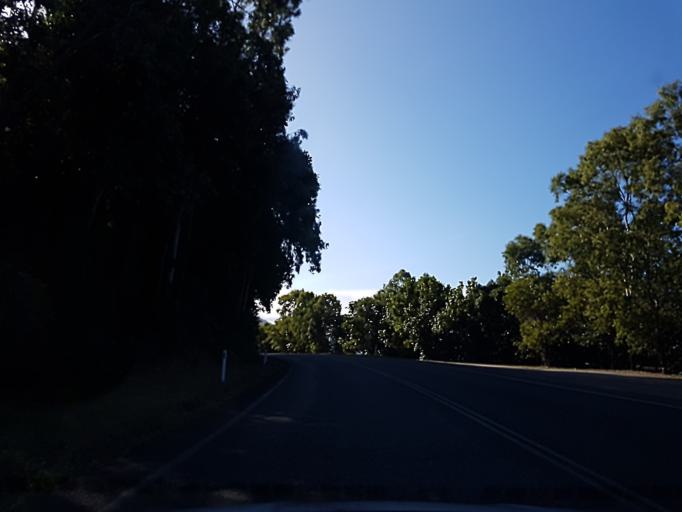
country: AU
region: Queensland
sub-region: Cairns
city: Port Douglas
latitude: -16.3876
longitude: 145.4184
